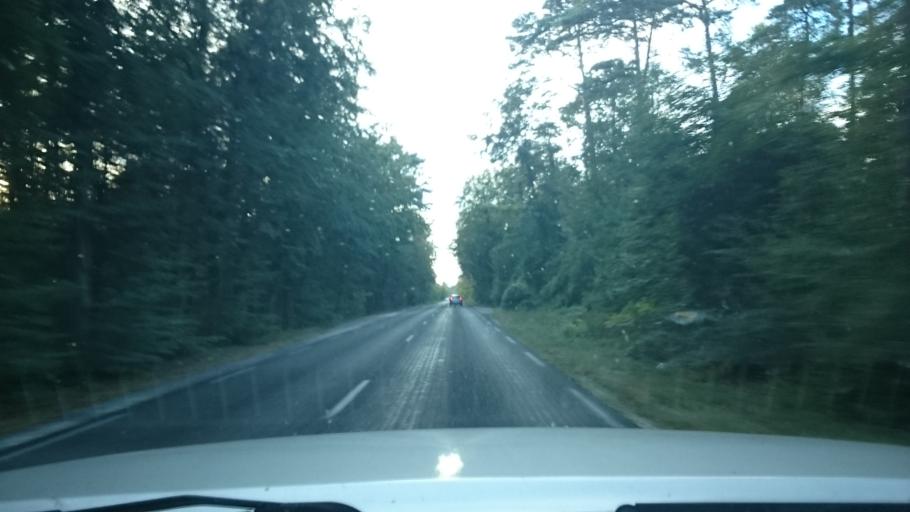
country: FR
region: Ile-de-France
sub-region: Departement de Seine-et-Marne
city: Samois-sur-Seine
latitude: 48.4387
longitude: 2.7294
